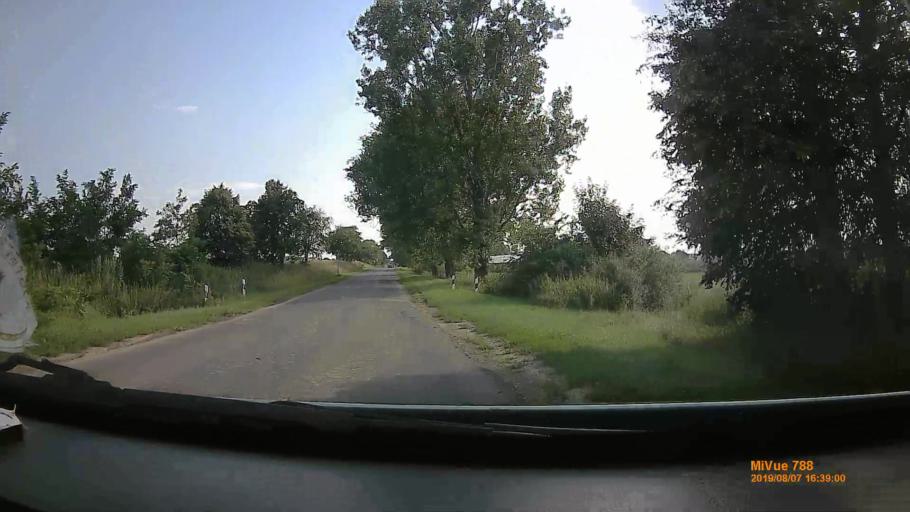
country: HU
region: Borsod-Abauj-Zemplen
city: Gonc
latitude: 48.3970
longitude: 21.2247
